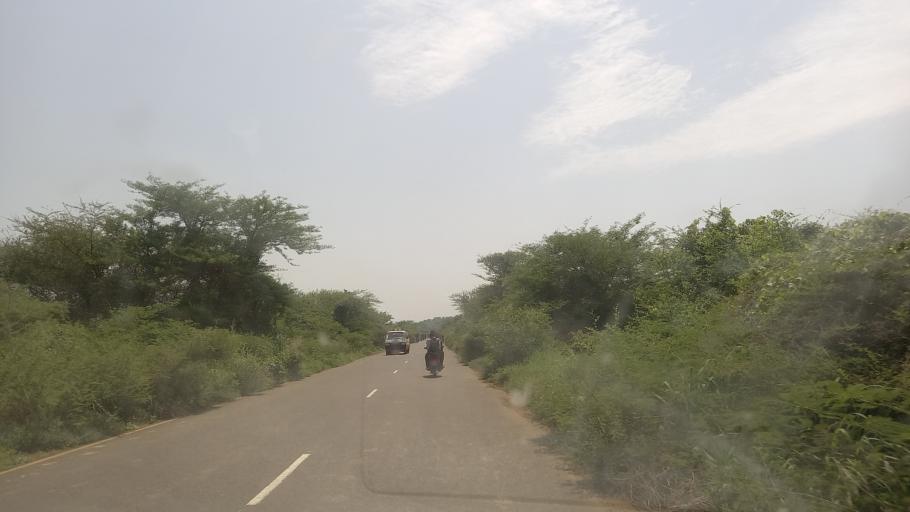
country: ET
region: Gambela
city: Gambela
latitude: 8.2795
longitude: 34.2270
